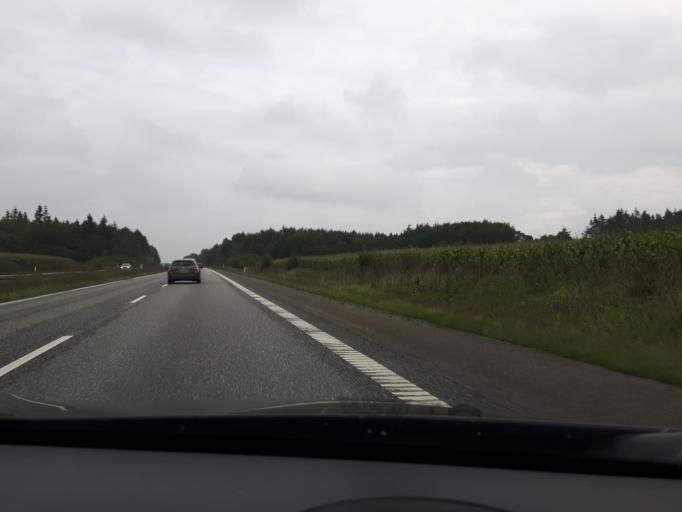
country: DK
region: North Denmark
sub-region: Mariagerfjord Kommune
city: Hobro
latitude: 56.6342
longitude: 9.7353
